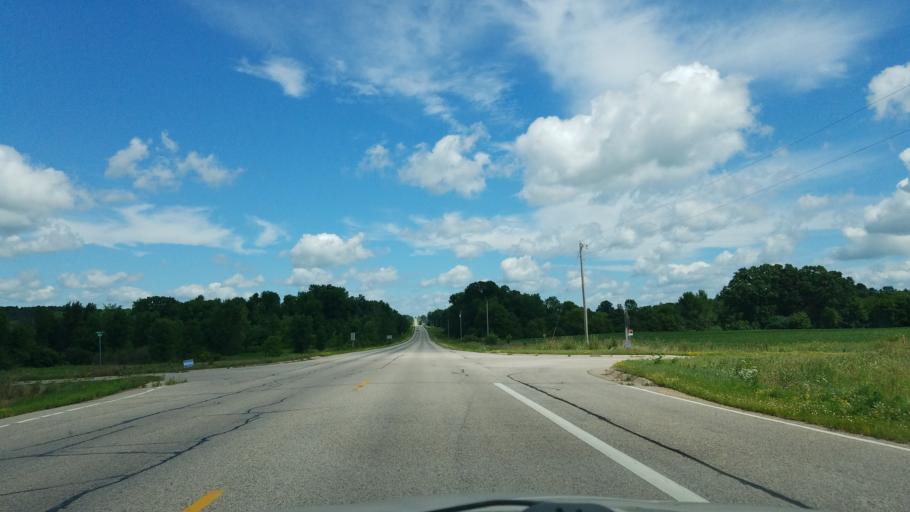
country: US
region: Wisconsin
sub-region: Saint Croix County
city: Glenwood City
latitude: 44.9877
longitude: -92.1965
